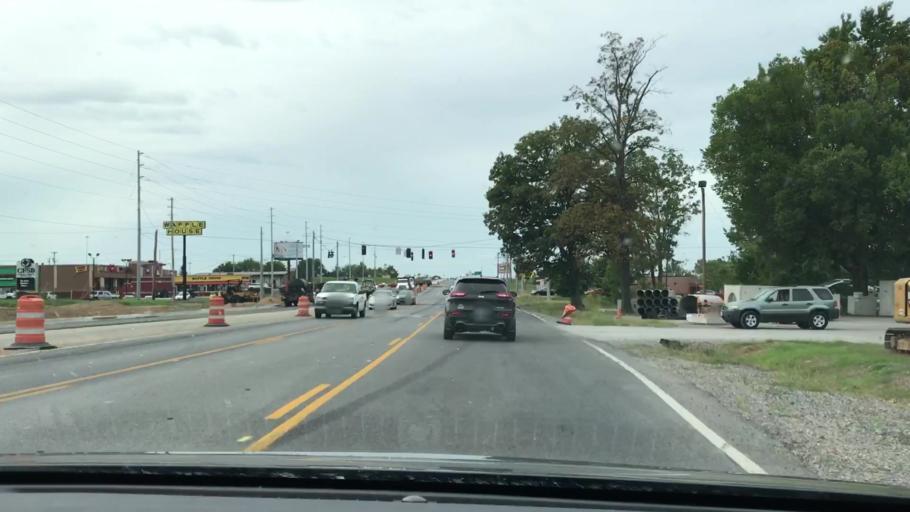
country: US
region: Kentucky
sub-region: Marshall County
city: Benton
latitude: 36.8667
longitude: -88.3589
